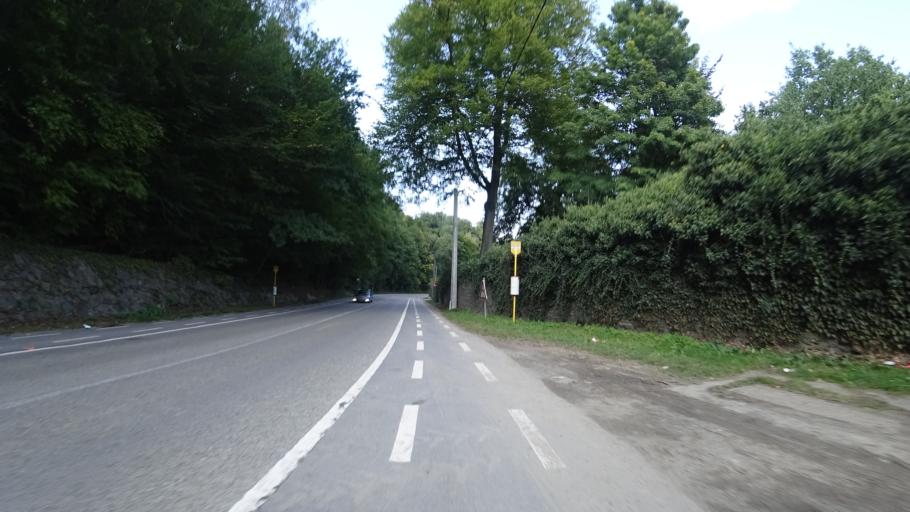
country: BE
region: Wallonia
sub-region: Province du Brabant Wallon
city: Villers-la-Ville
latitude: 50.5912
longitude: 4.5275
